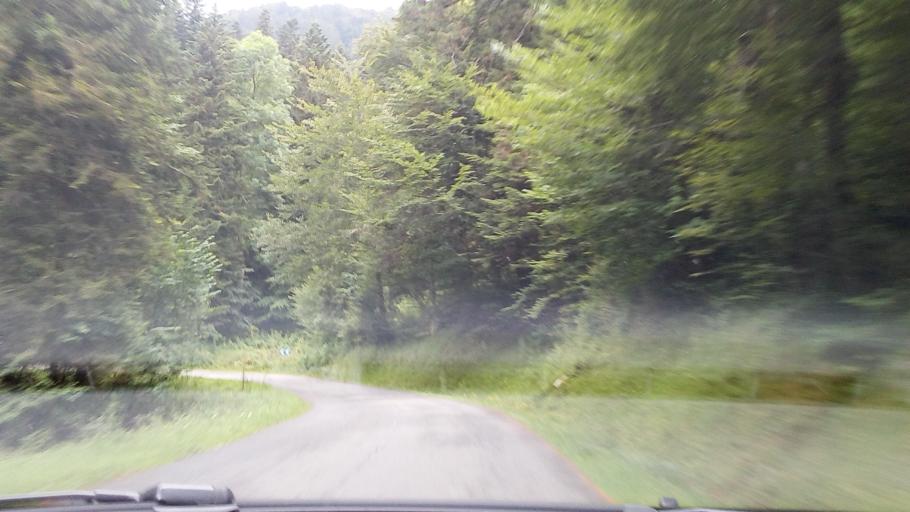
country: FR
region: Aquitaine
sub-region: Departement des Pyrenees-Atlantiques
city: Ogeu-les-Bains
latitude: 43.0655
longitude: -0.5016
